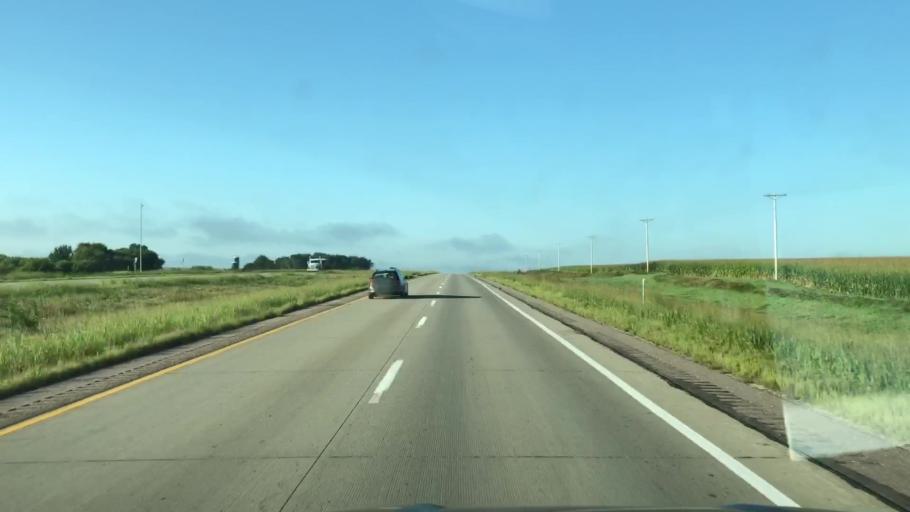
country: US
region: Iowa
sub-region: Sioux County
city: Alton
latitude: 42.9505
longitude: -96.0365
